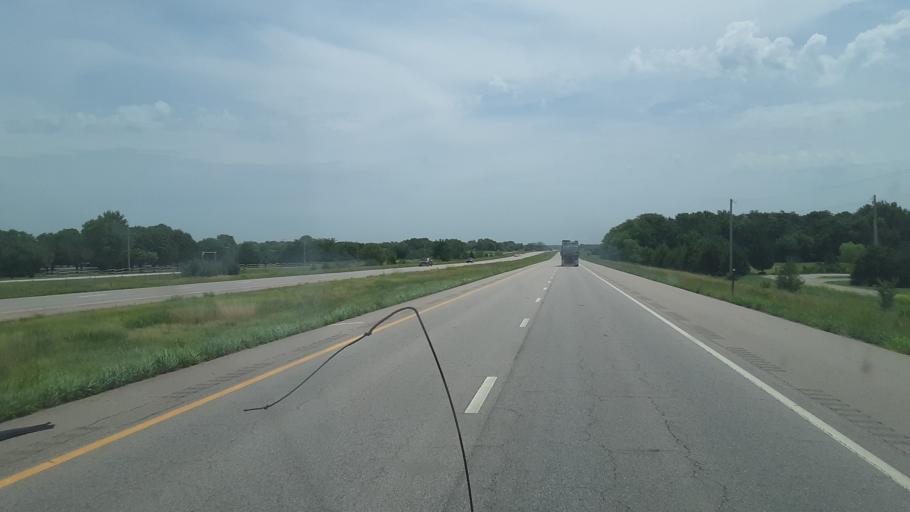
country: US
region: Kansas
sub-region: Butler County
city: Towanda
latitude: 37.7959
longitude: -97.0496
